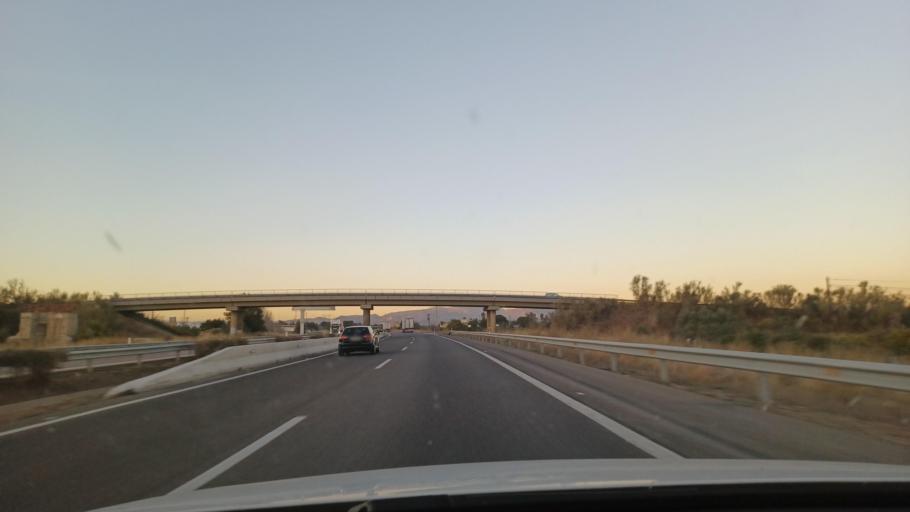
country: ES
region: Valencia
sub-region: Provincia de Castello
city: Vila-real
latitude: 39.9501
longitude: -0.1295
